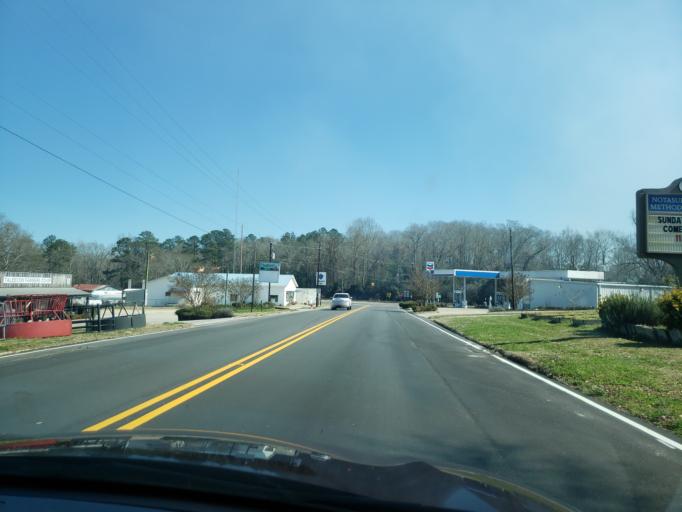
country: US
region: Alabama
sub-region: Macon County
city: Tuskegee
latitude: 32.5624
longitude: -85.6709
